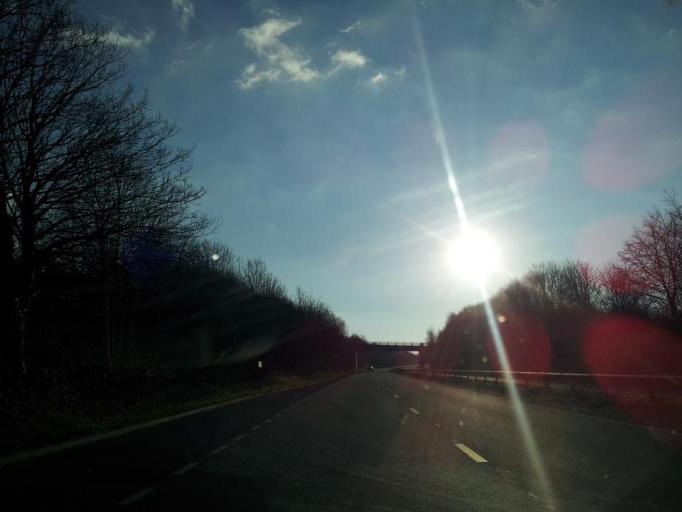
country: GB
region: England
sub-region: Cornwall
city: Launceston
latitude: 50.6343
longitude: -4.3300
